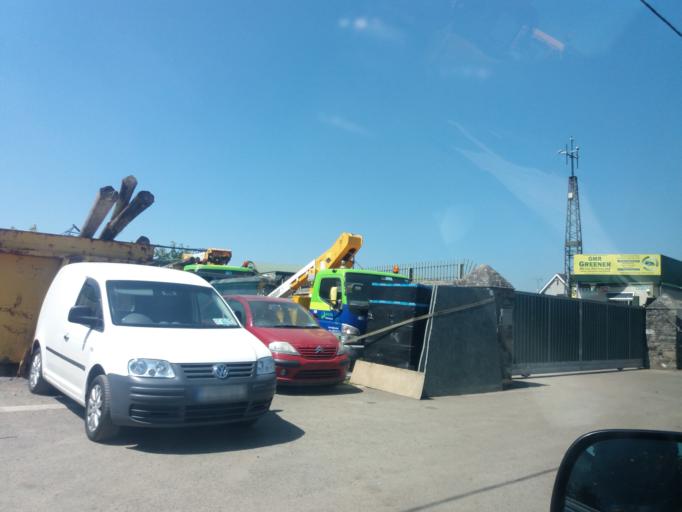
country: IE
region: Leinster
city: Lusk
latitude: 53.5306
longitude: -6.2365
